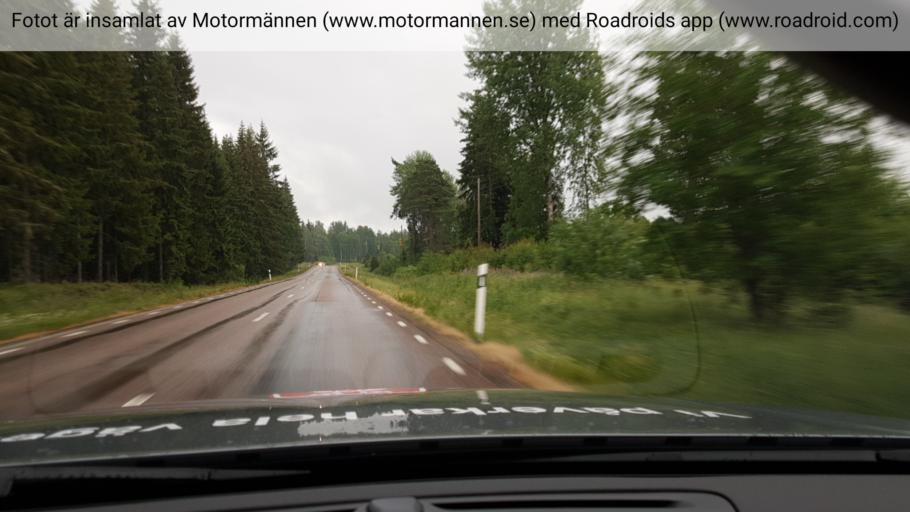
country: SE
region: Vaestmanland
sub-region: Norbergs Kommun
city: Norberg
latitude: 60.0220
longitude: 16.0239
